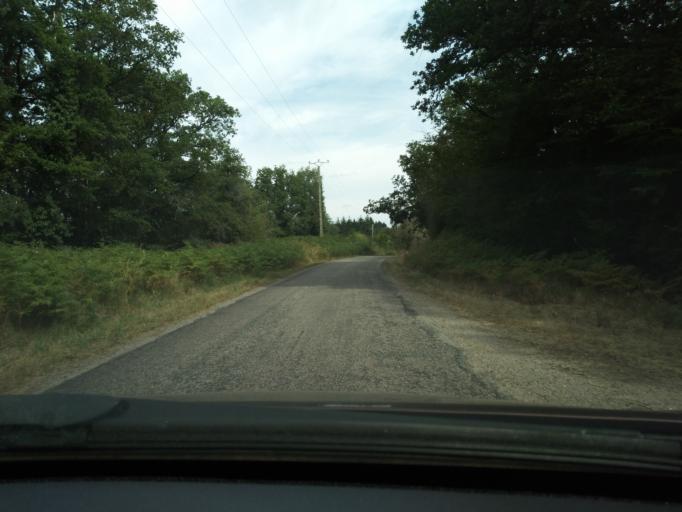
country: FR
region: Bourgogne
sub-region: Departement de la Cote-d'Or
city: Saulieu
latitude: 47.3795
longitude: 4.0773
